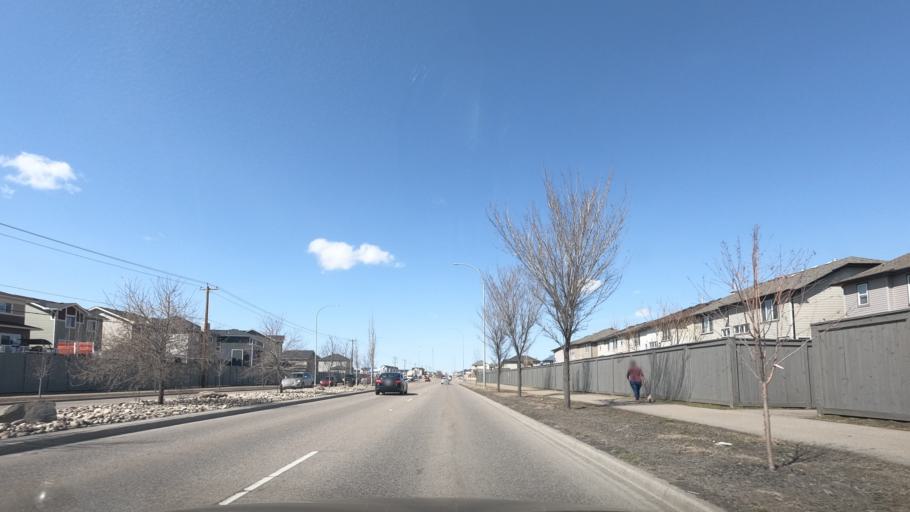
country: CA
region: Alberta
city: Airdrie
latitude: 51.2771
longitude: -114.0251
